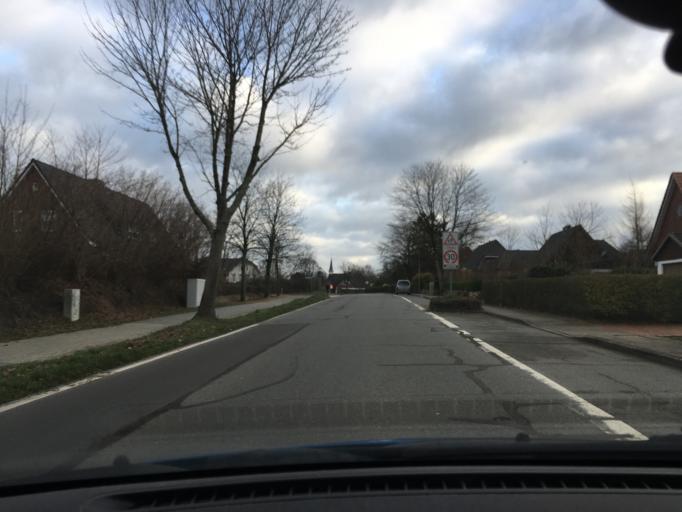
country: DE
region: Schleswig-Holstein
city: Schenefeld
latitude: 54.0478
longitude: 9.4749
